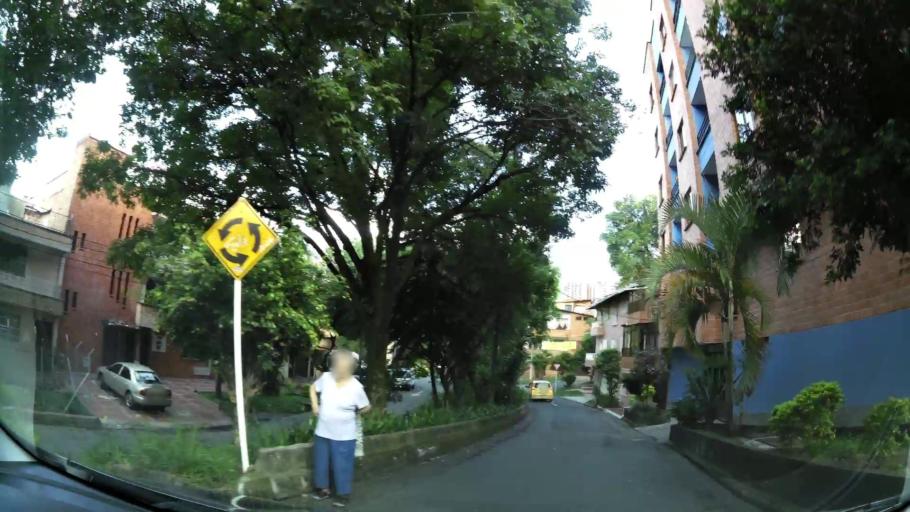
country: CO
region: Antioquia
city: Envigado
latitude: 6.1708
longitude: -75.5818
